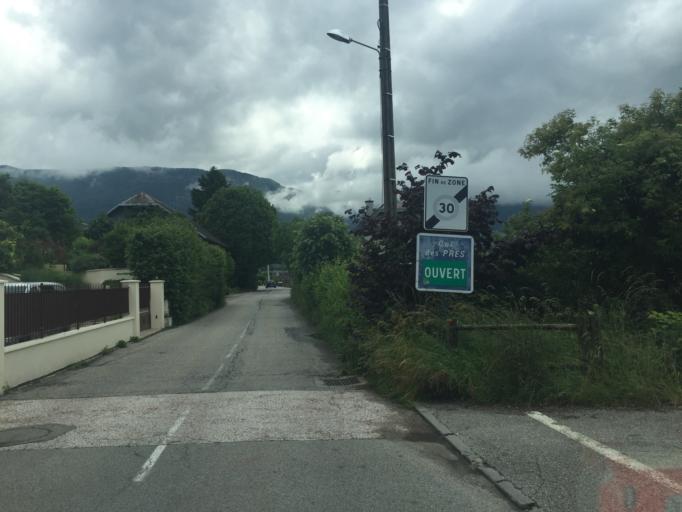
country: FR
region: Rhone-Alpes
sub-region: Departement de la Savoie
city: Barby
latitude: 45.5860
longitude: 5.9973
